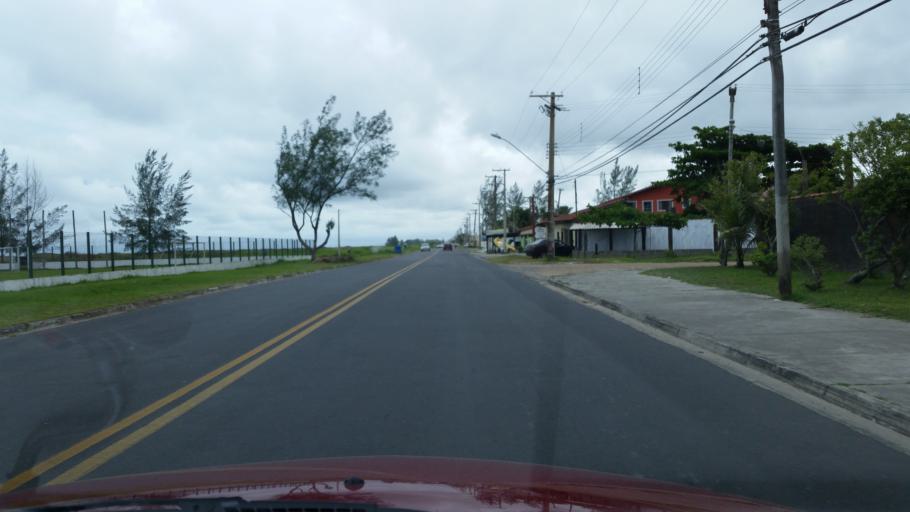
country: BR
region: Sao Paulo
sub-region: Iguape
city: Iguape
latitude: -24.7551
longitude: -47.5617
